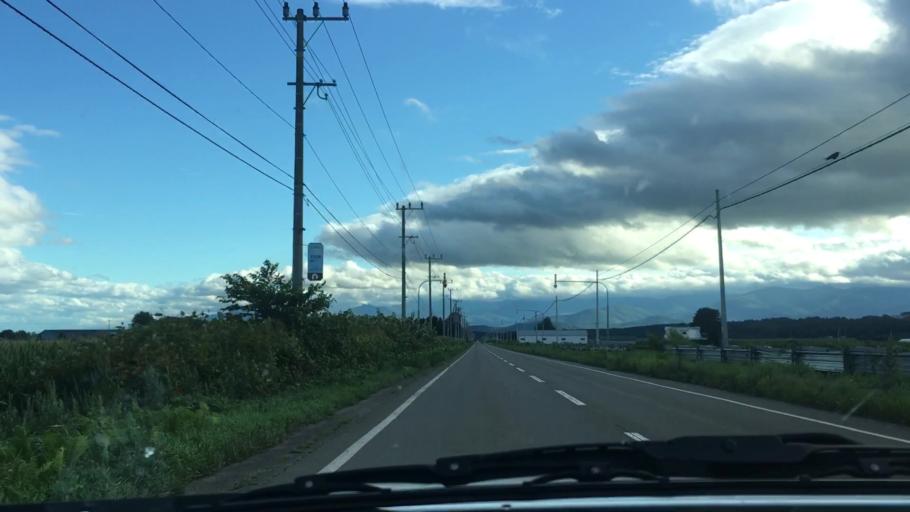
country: JP
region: Hokkaido
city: Otofuke
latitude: 43.1571
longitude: 142.9028
